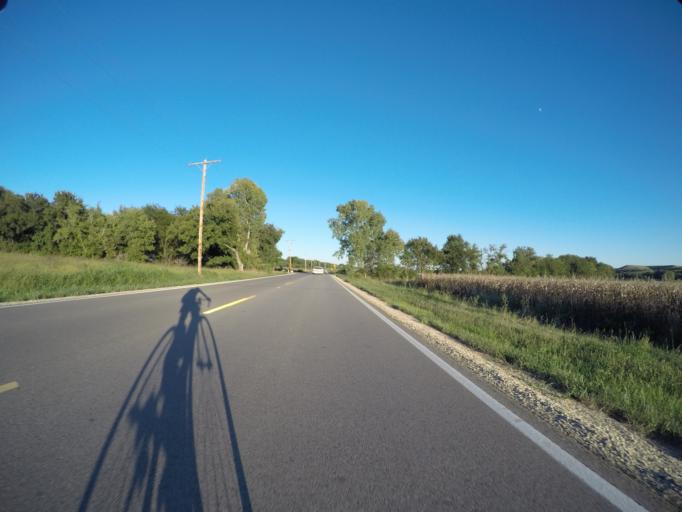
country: US
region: Kansas
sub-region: Riley County
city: Ogden
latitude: 39.2166
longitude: -96.6918
